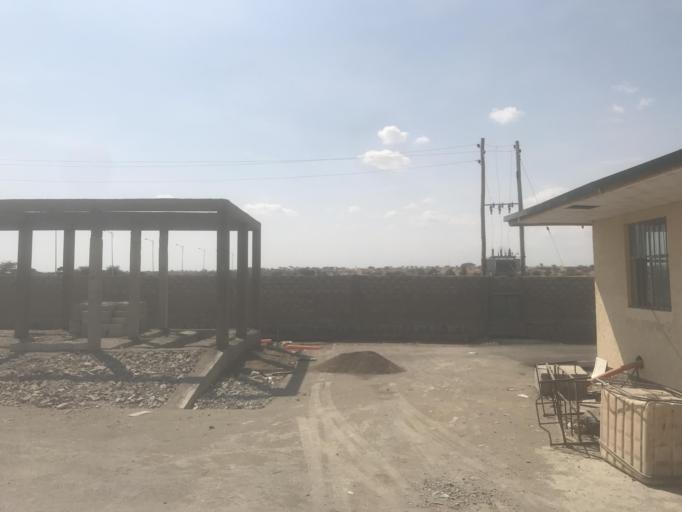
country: ET
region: Oromiya
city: Ziway
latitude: 8.1452
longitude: 38.7964
